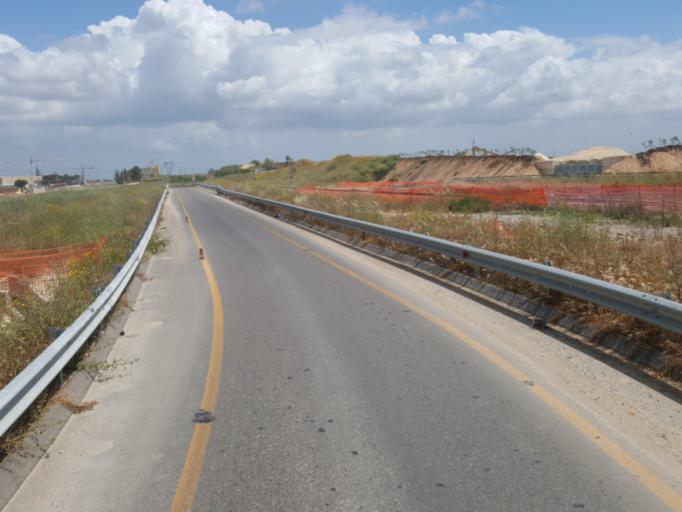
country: IT
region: Apulia
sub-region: Provincia di Bari
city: Palo del Colle
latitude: 41.0667
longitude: 16.7281
